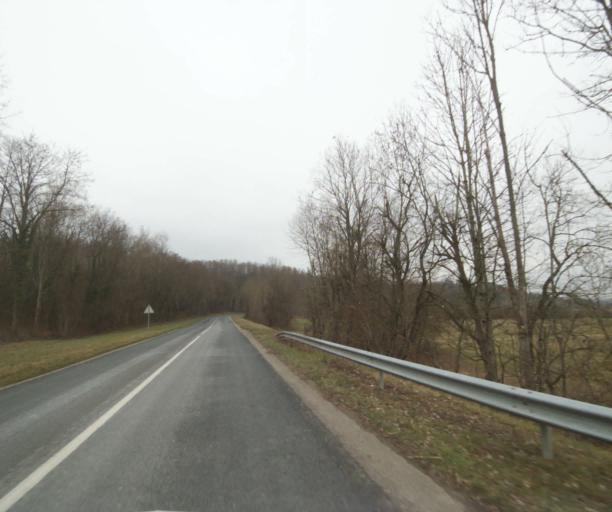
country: FR
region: Champagne-Ardenne
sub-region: Departement de la Haute-Marne
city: Bienville
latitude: 48.5685
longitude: 5.0401
